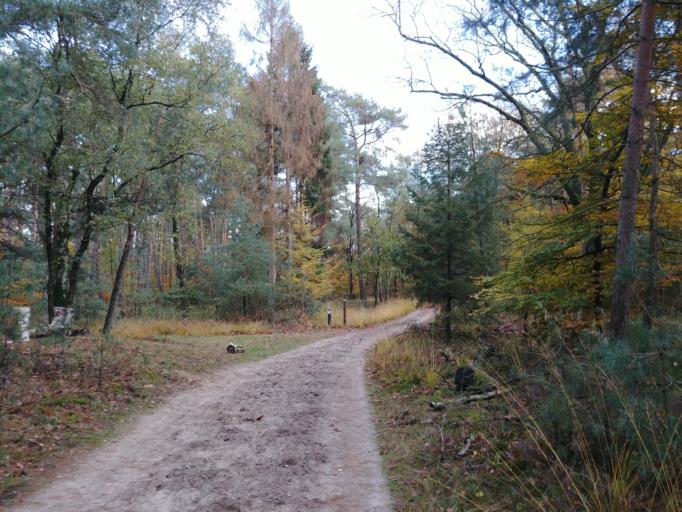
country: NL
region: Gelderland
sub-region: Gemeente Rheden
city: De Steeg
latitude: 52.0601
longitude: 6.0424
